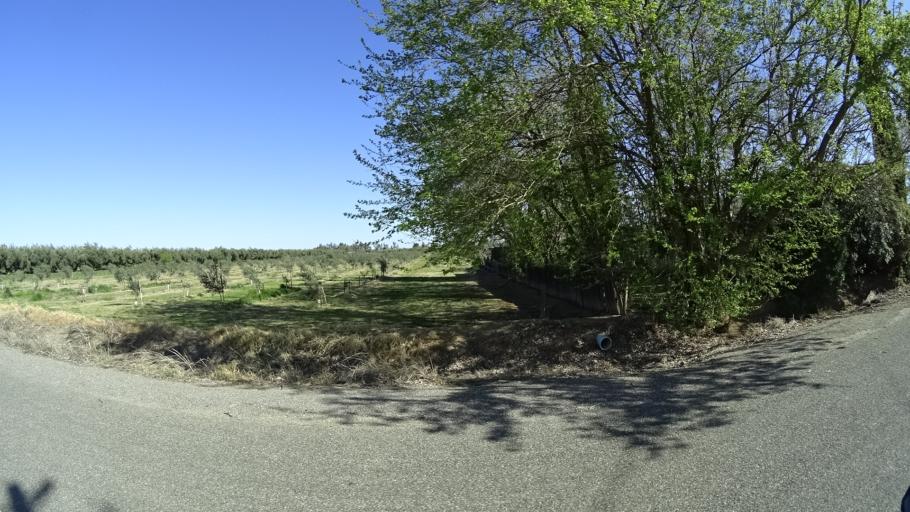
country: US
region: California
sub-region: Glenn County
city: Orland
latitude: 39.7476
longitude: -122.2291
